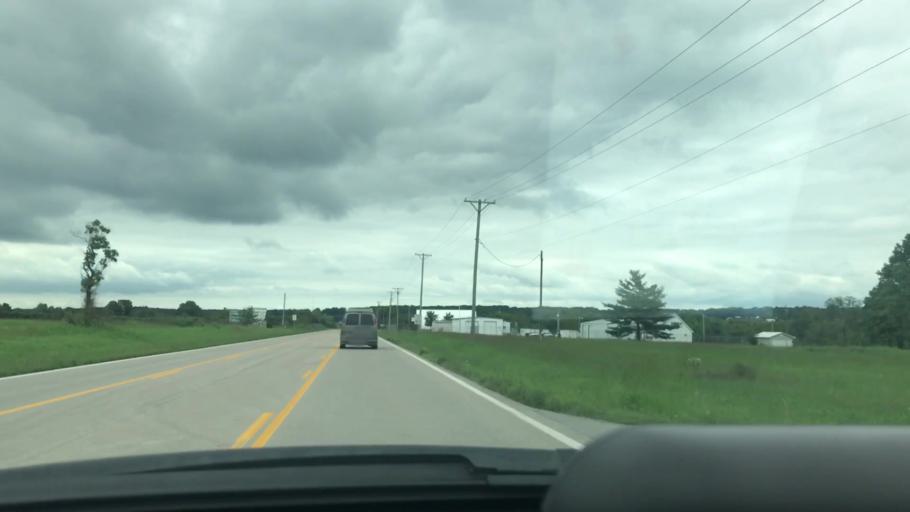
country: US
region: Missouri
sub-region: Dallas County
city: Buffalo
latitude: 37.6569
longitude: -93.1037
